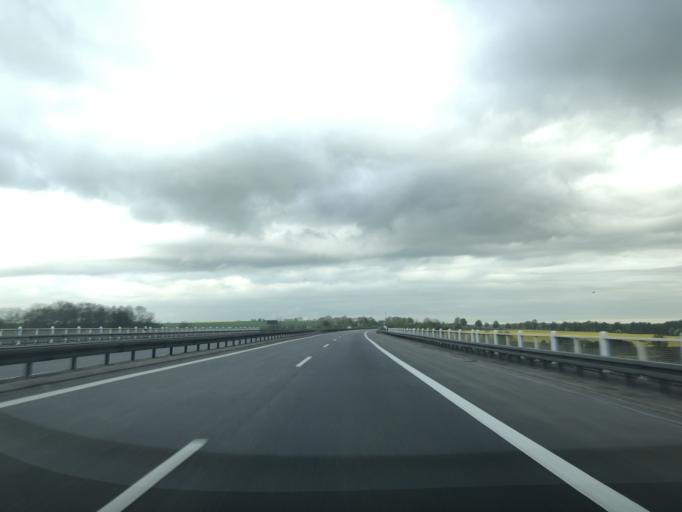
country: DE
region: Mecklenburg-Vorpommern
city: Tessin
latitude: 54.0135
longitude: 12.4477
